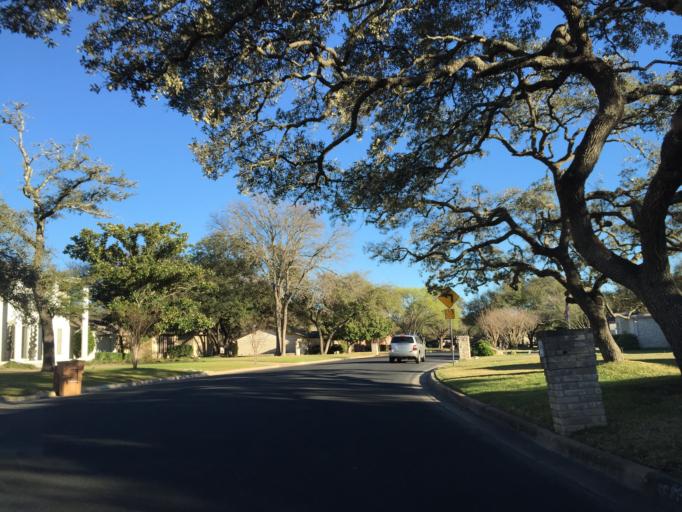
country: US
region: Texas
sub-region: Williamson County
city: Jollyville
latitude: 30.4393
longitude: -97.7902
